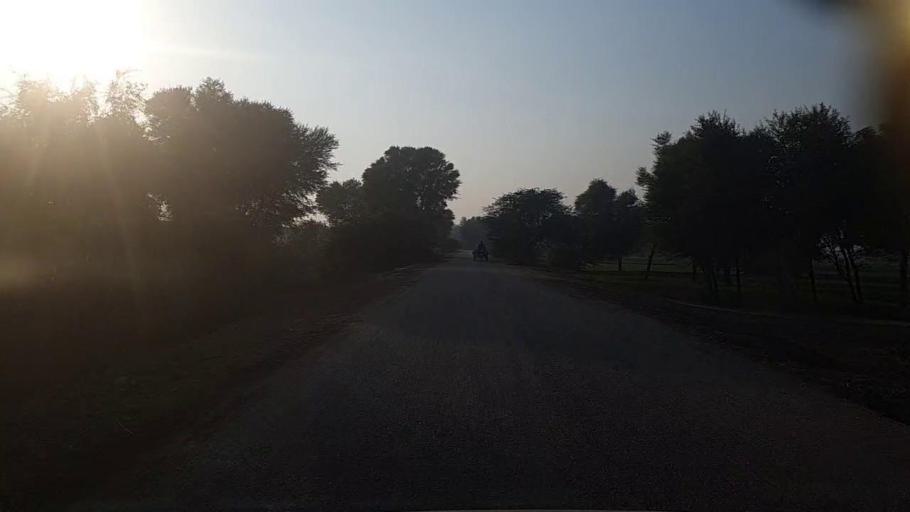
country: PK
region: Sindh
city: Pad Idan
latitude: 26.7181
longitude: 68.4082
